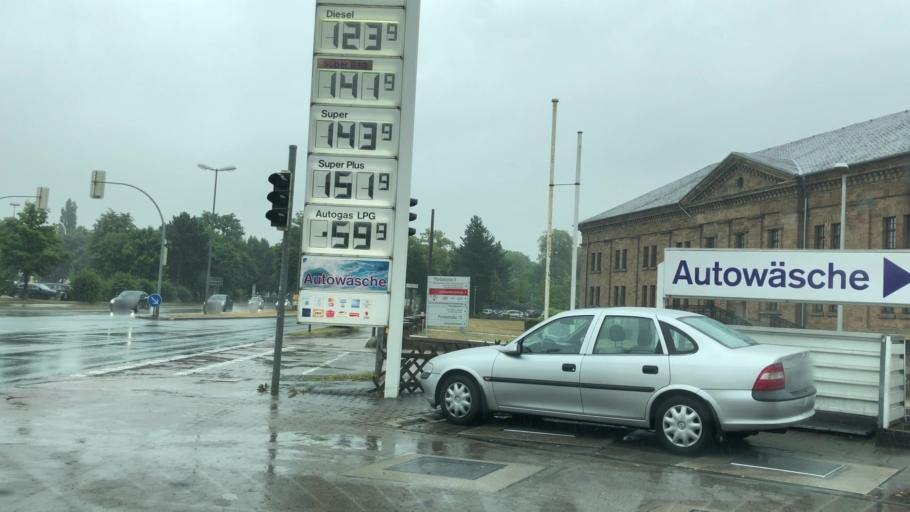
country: DE
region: North Rhine-Westphalia
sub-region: Regierungsbezirk Detmold
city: Minden
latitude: 52.3053
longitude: 8.9091
